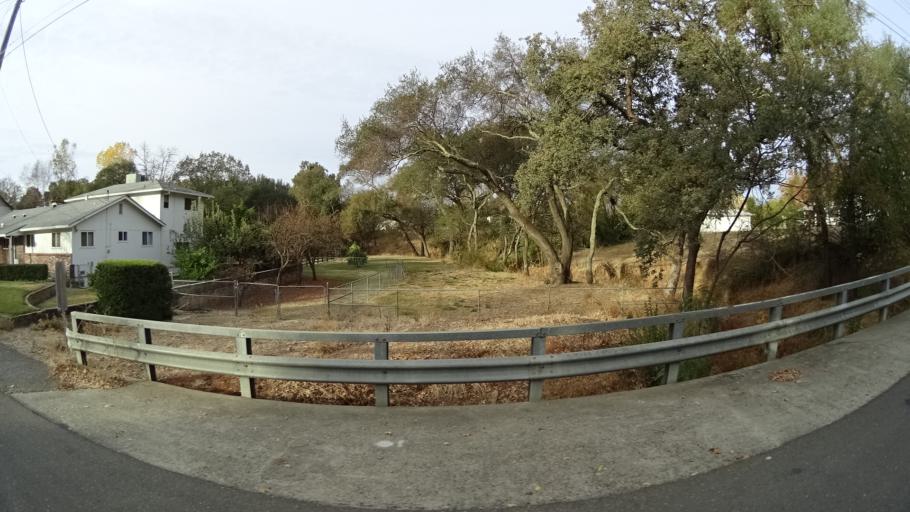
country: US
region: California
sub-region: Sacramento County
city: Citrus Heights
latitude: 38.7174
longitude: -121.2766
